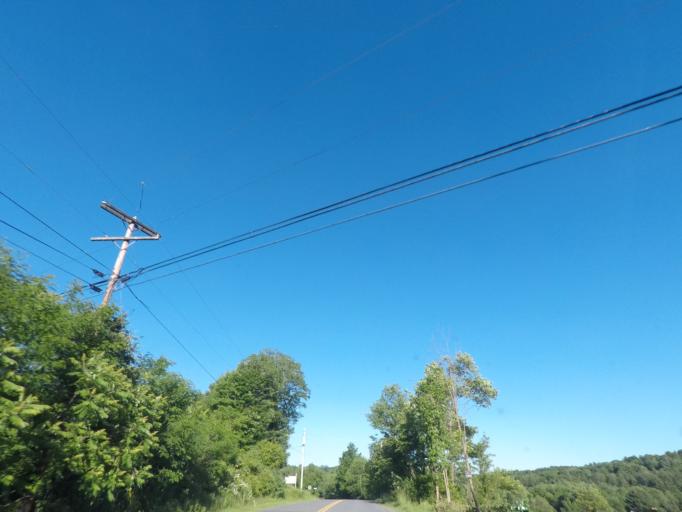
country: US
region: New York
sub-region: Rensselaer County
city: Averill Park
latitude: 42.5798
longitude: -73.5452
